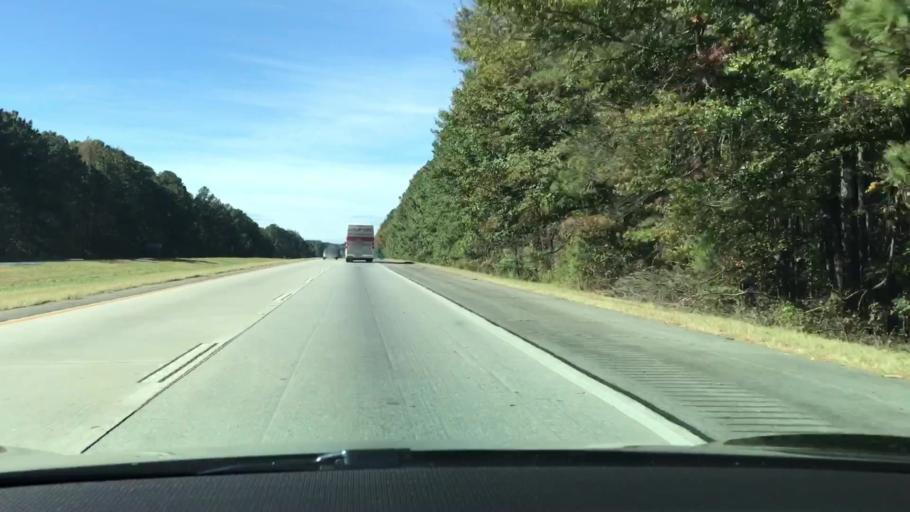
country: US
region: Georgia
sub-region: Greene County
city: Union Point
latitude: 33.5485
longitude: -83.0625
